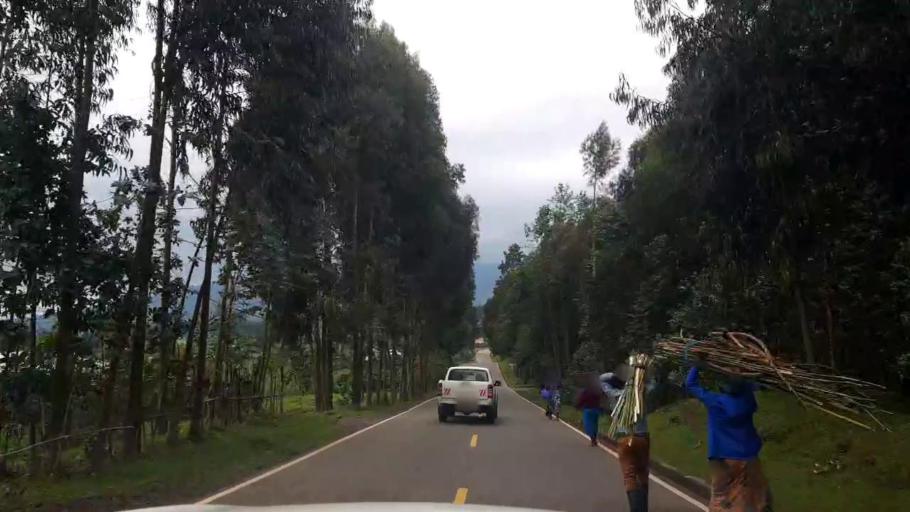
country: RW
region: Northern Province
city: Musanze
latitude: -1.4344
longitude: 29.5565
